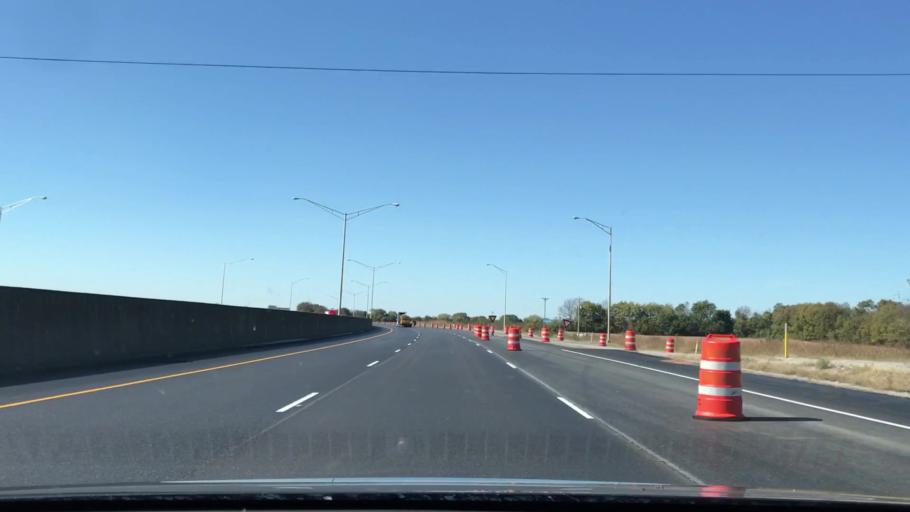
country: US
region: Kentucky
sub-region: Edmonson County
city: Brownsville
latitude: 37.0423
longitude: -86.2120
